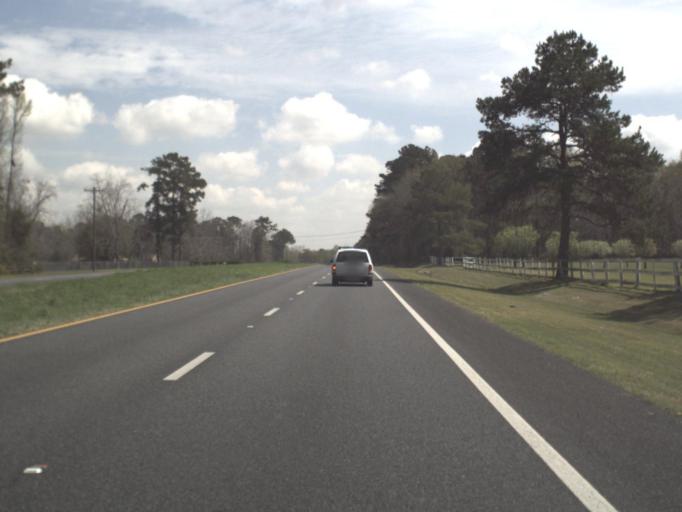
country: US
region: Florida
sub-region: Gadsden County
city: Havana
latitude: 30.6724
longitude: -84.3940
